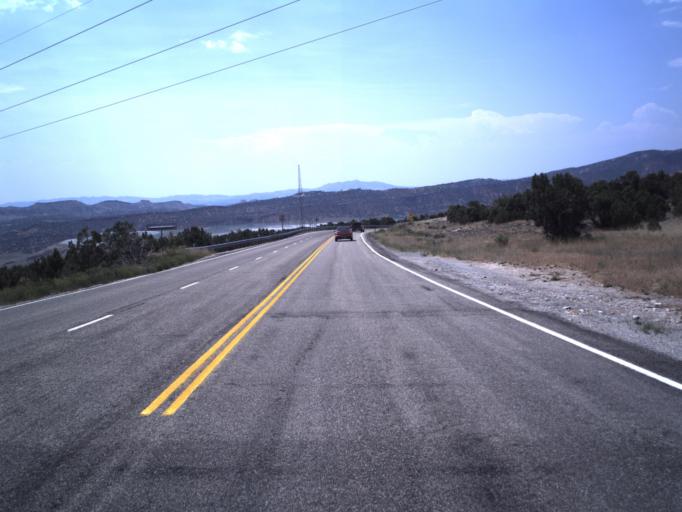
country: US
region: Utah
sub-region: Uintah County
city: Vernal
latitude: 40.6220
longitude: -109.4735
